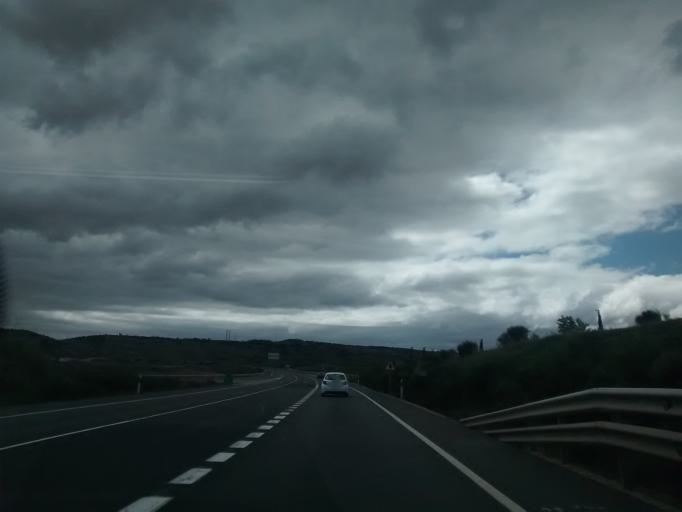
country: ES
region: La Rioja
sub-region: Provincia de La Rioja
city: Ausejo
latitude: 42.3451
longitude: -2.1788
